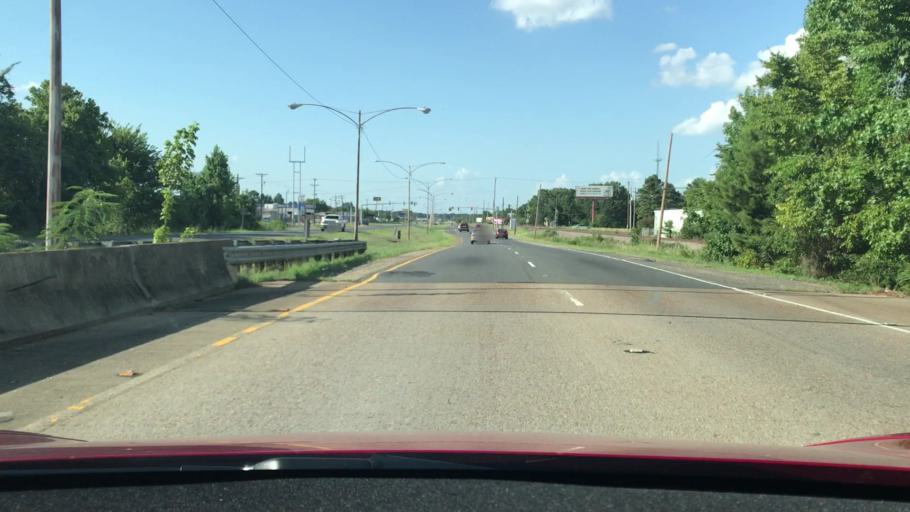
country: US
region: Louisiana
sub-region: Bossier Parish
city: Bossier City
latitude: 32.4333
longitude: -93.7836
